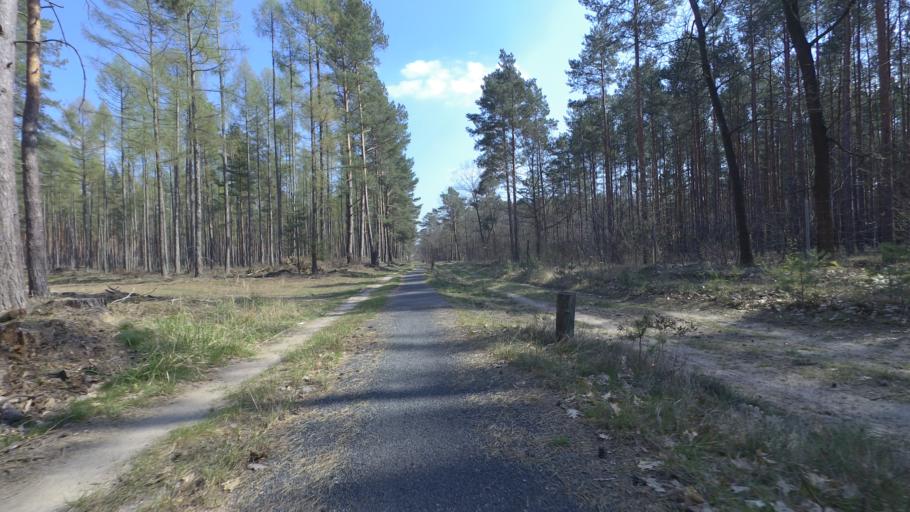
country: DE
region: Brandenburg
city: Mittenwalde
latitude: 52.1868
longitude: 13.5387
